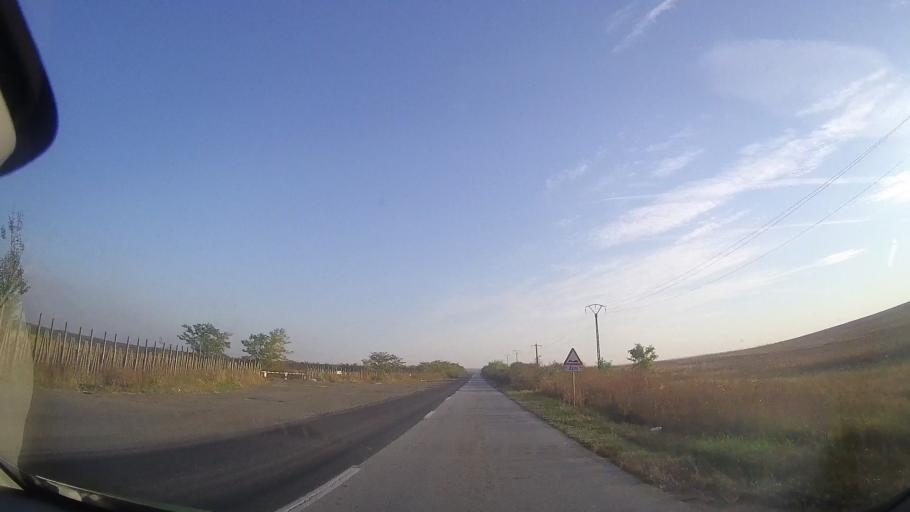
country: RO
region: Timis
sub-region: Comuna Giarmata
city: Giarmata
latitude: 45.8655
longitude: 21.3186
